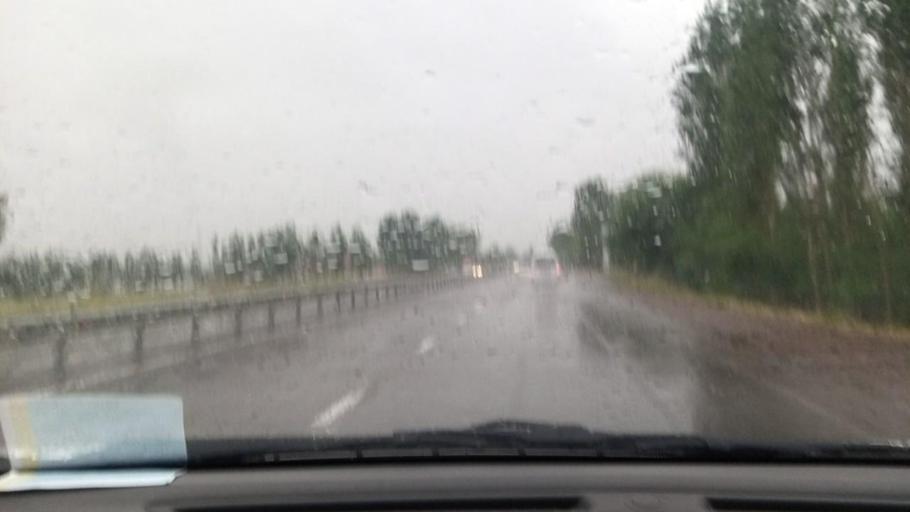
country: UZ
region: Toshkent
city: Ohangaron
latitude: 40.9089
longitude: 69.7609
